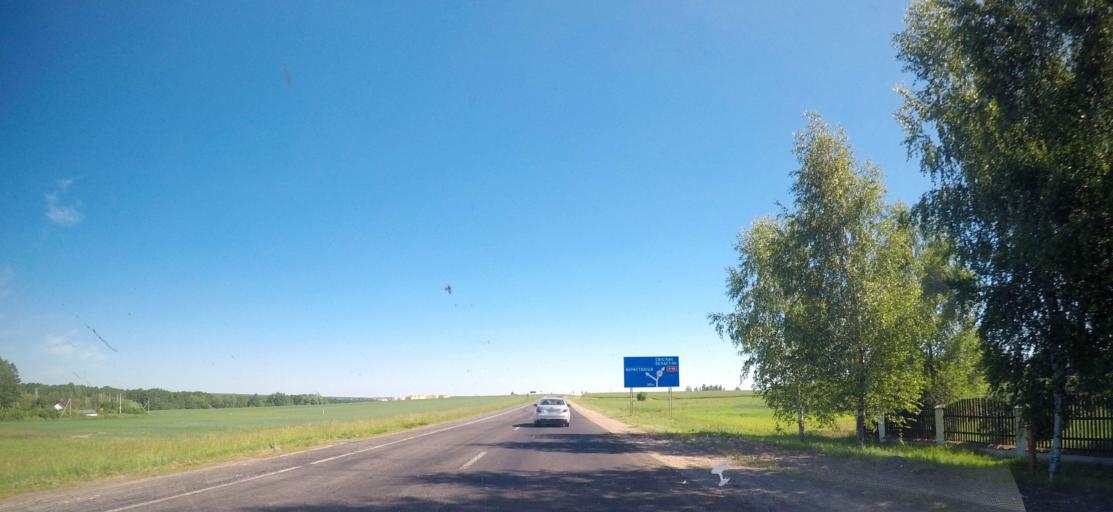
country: BY
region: Grodnenskaya
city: Vyalikaya Byerastavitsa
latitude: 53.2111
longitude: 24.0039
